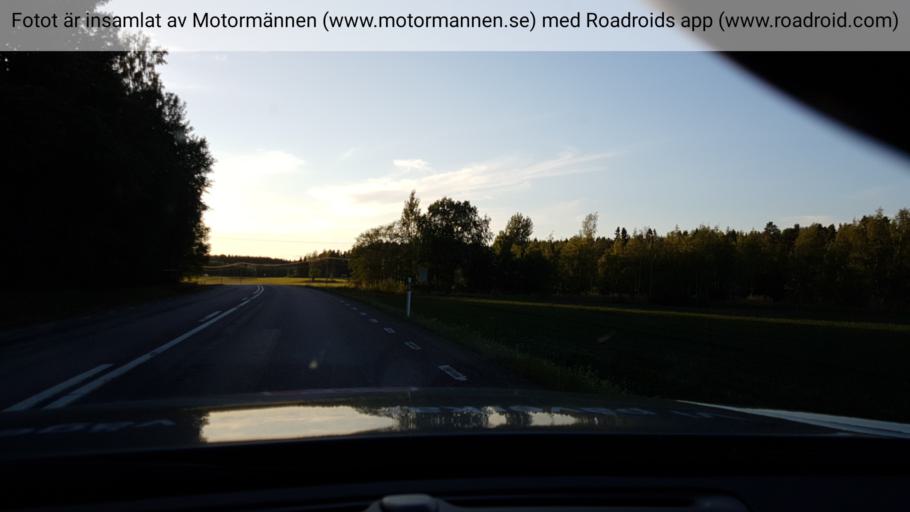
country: SE
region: OErebro
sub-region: Karlskoga Kommun
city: Karlskoga
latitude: 59.3895
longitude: 14.4707
